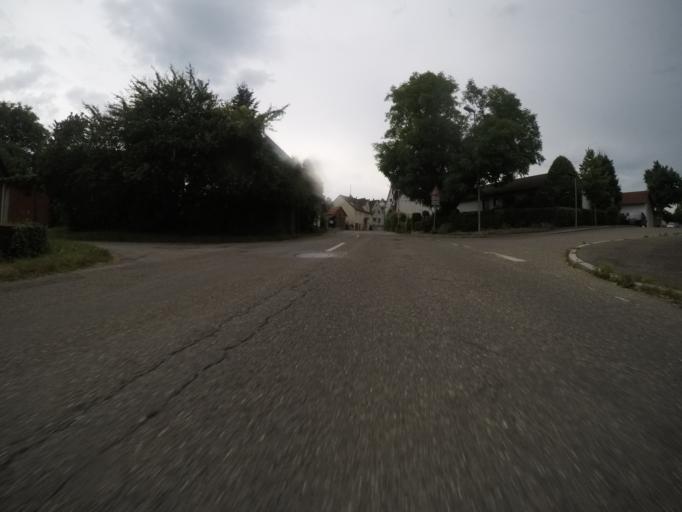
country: DE
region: Baden-Wuerttemberg
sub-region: Regierungsbezirk Stuttgart
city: Eberdingen
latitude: 48.8556
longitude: 8.9829
